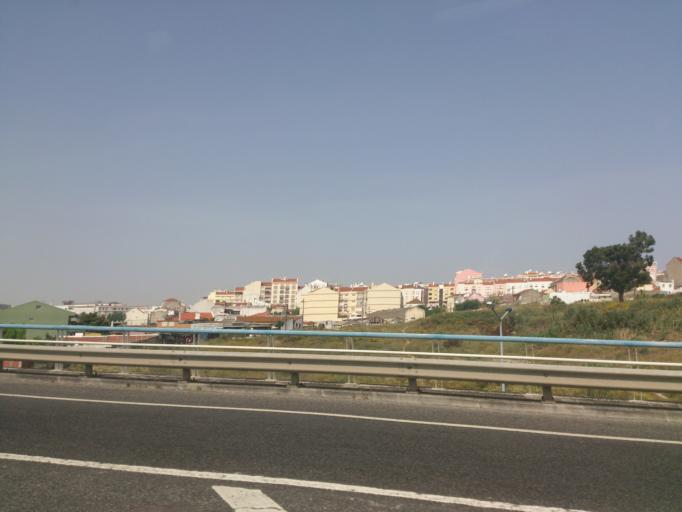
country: PT
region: Lisbon
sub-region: Loures
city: Sacavem
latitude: 38.7908
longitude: -9.1161
